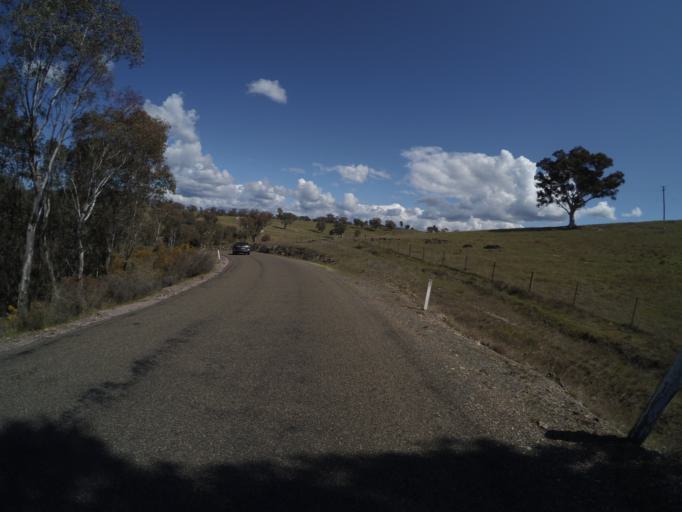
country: AU
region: New South Wales
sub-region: Yass Valley
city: Murrumbateman
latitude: -35.0664
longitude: 148.8358
